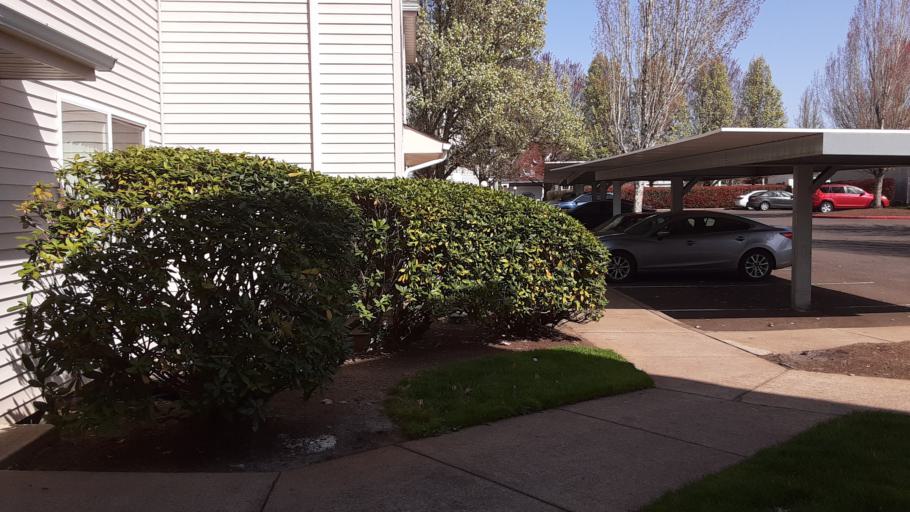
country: US
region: Oregon
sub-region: Benton County
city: Corvallis
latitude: 44.5342
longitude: -123.2577
